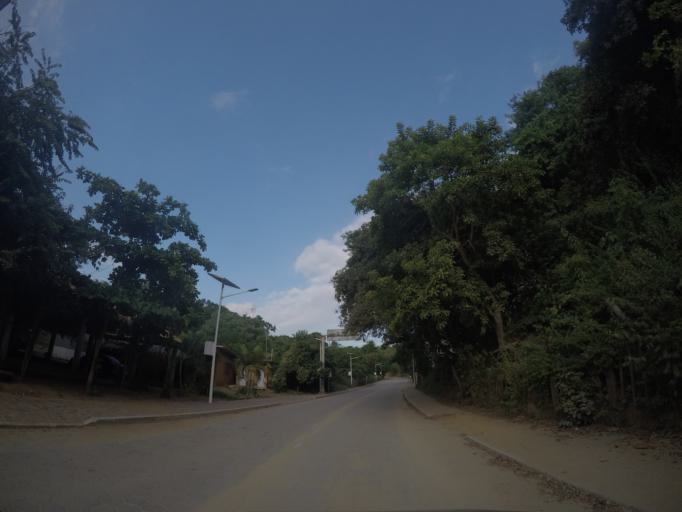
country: MX
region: Oaxaca
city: Santa Maria Tonameca
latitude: 15.6669
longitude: -96.5507
